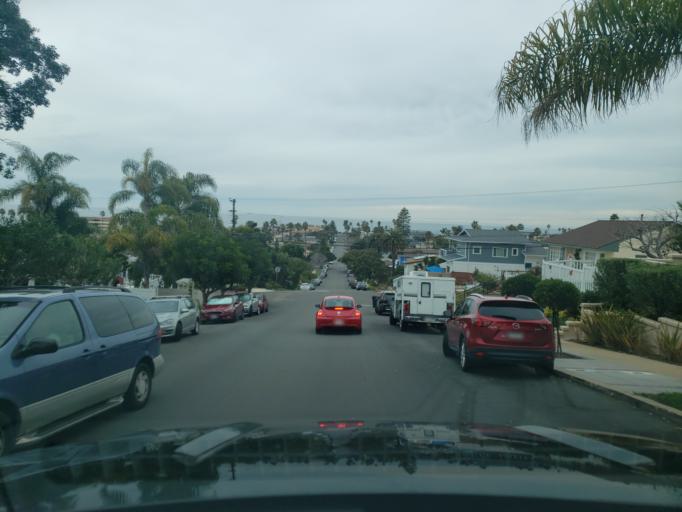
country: US
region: California
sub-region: San Diego County
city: Coronado
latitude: 32.7383
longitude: -117.2497
